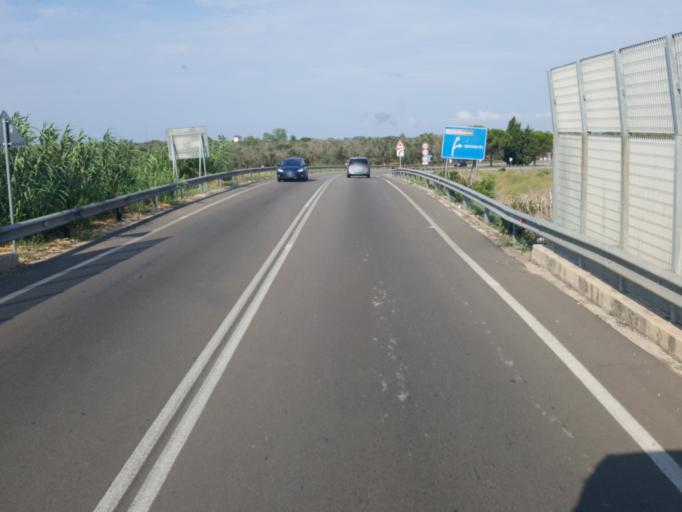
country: IT
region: Apulia
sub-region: Provincia di Lecce
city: Trepuzzi
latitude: 40.4397
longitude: 18.0782
